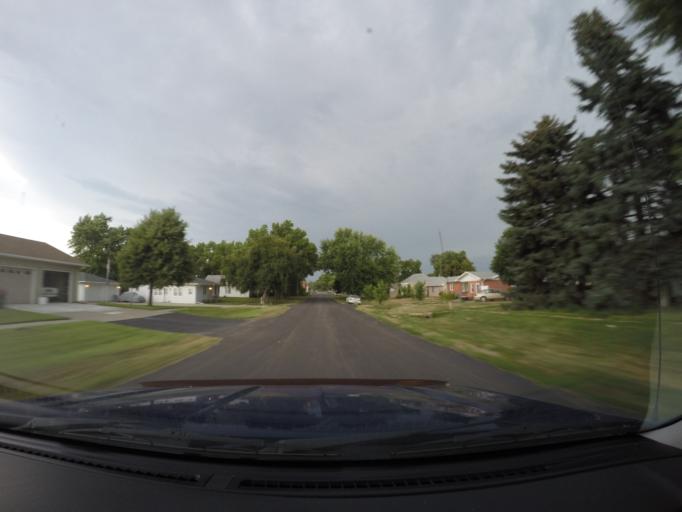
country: US
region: Nebraska
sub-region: Buffalo County
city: Kearney
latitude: 40.8383
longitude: -99.2677
